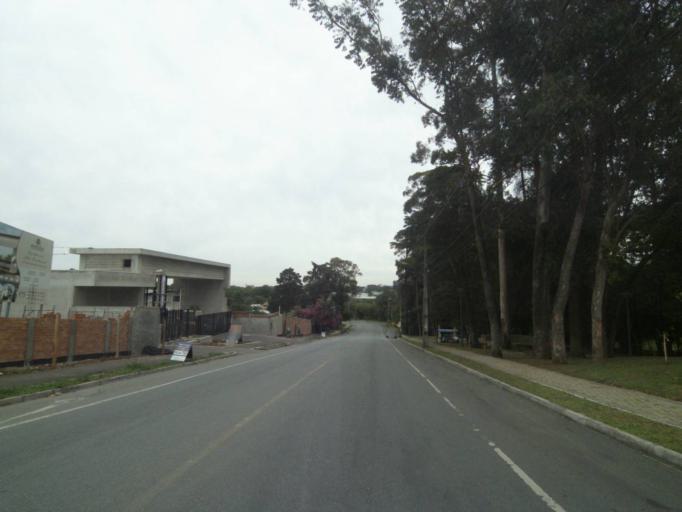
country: BR
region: Parana
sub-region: Pinhais
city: Pinhais
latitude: -25.4113
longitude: -49.2174
